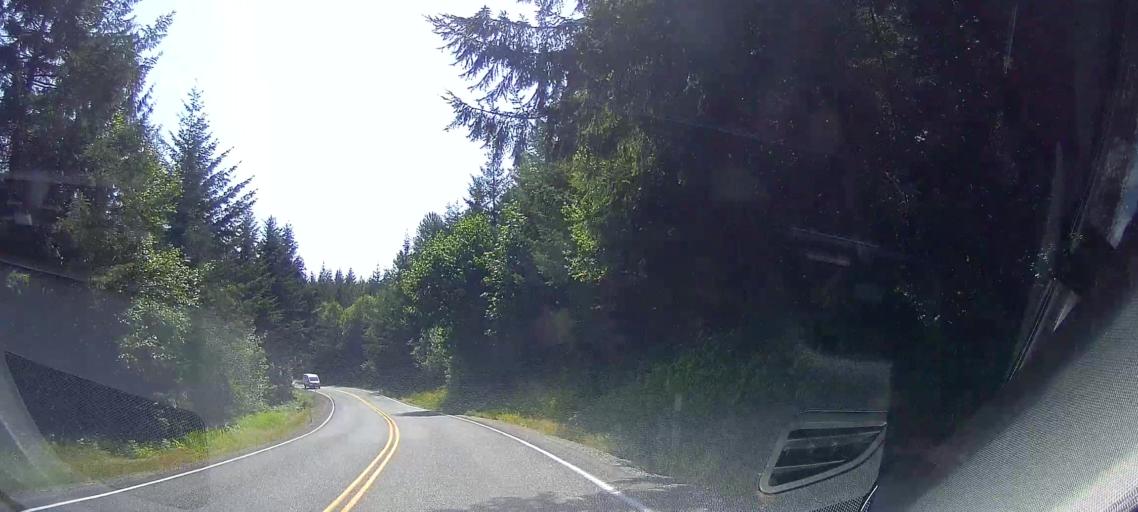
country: US
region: Washington
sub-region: Snohomish County
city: Bryant
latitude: 48.3372
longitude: -122.1244
